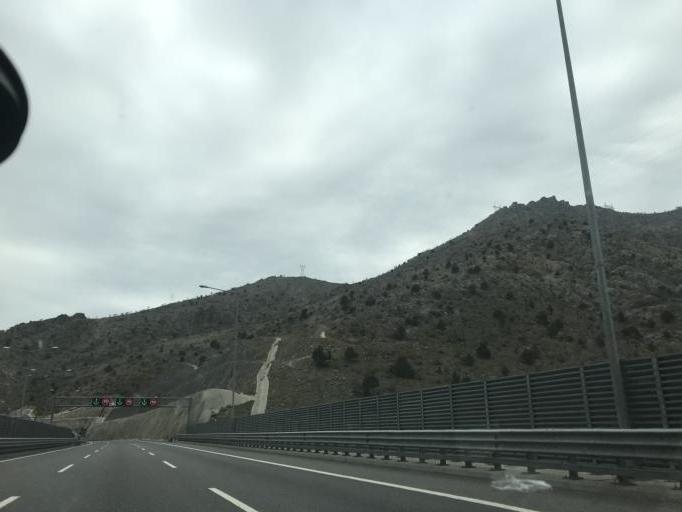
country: TR
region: Nigde
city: Ciftehan
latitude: 37.5463
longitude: 34.7845
